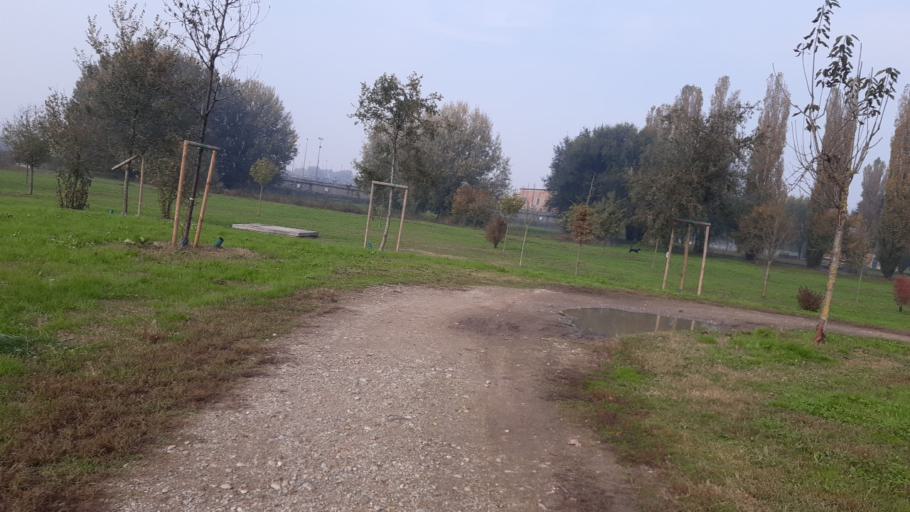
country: IT
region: Lombardy
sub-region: Citta metropolitana di Milano
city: Chiaravalle
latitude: 45.4211
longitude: 9.2252
